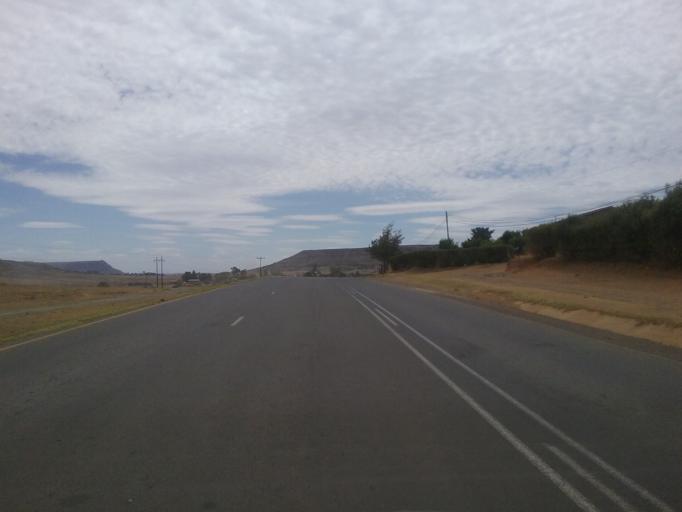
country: LS
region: Maseru
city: Nako
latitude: -29.6324
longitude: 27.4815
